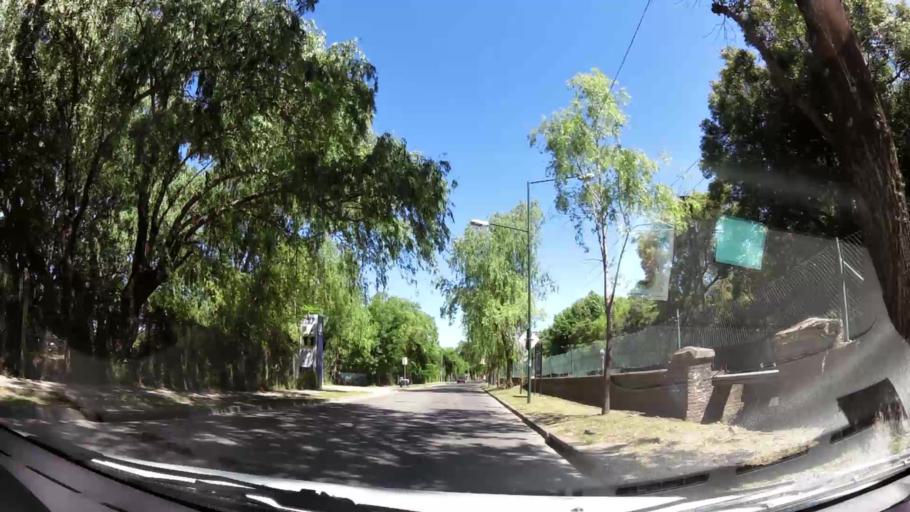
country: AR
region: Buenos Aires
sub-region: Partido de Vicente Lopez
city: Olivos
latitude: -34.4829
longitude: -58.4820
